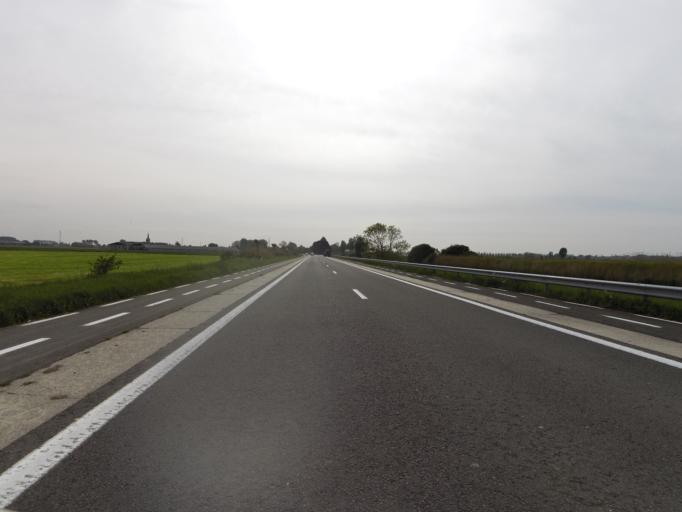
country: BE
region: Flanders
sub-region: Provincie West-Vlaanderen
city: Nieuwpoort
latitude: 51.1078
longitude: 2.7092
